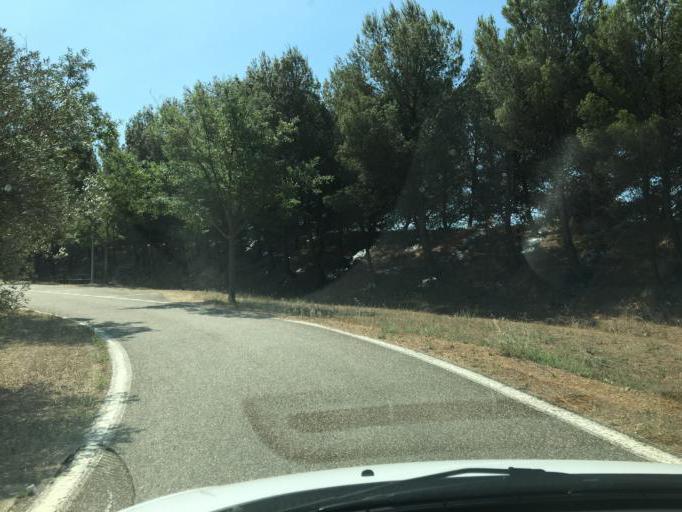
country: FR
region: Provence-Alpes-Cote d'Azur
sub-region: Departement des Bouches-du-Rhone
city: La Fare-les-Oliviers
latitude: 43.5871
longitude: 5.1905
